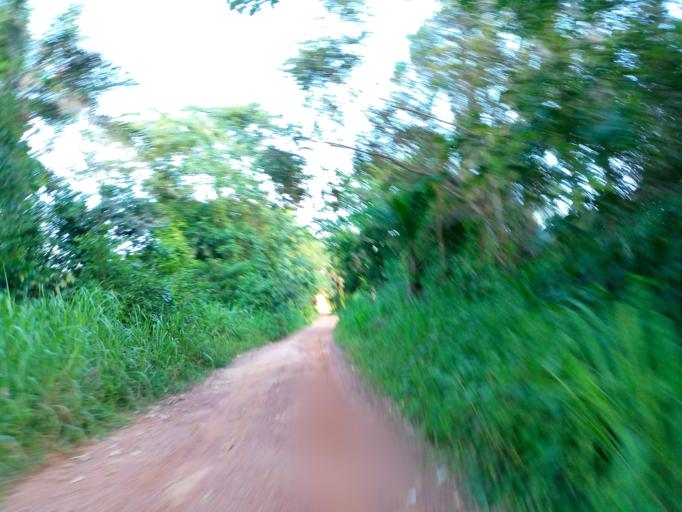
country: SL
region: Northern Province
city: Yonibana
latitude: 8.4553
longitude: -12.2464
